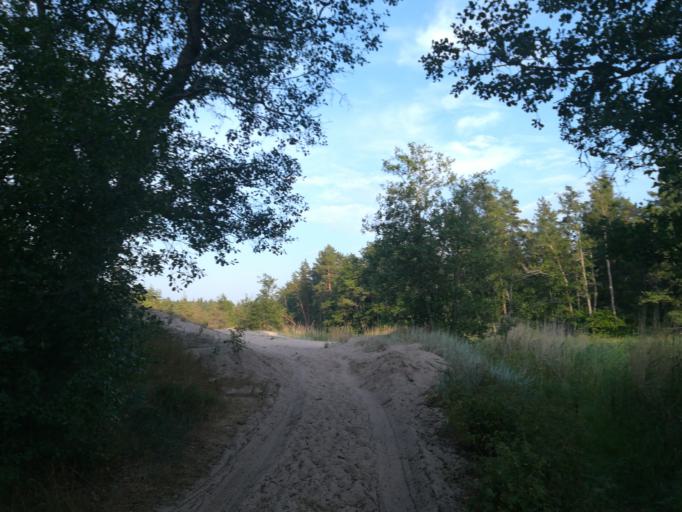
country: RU
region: Leningrad
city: Ust'-Luga
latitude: 59.6772
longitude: 28.2421
